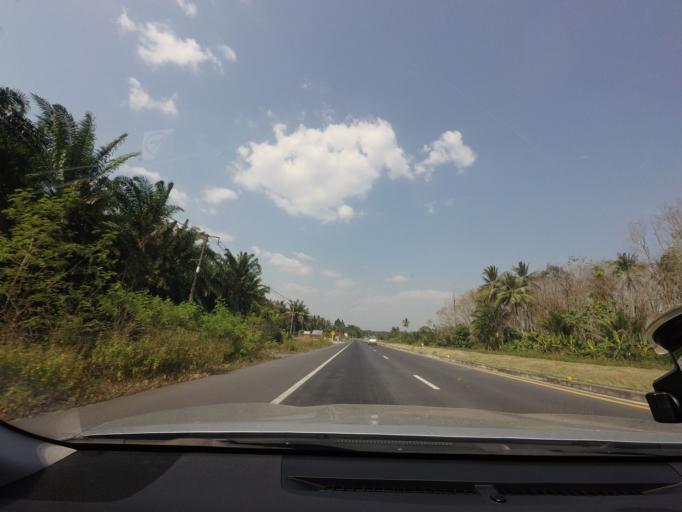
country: TH
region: Phangnga
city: Thap Put
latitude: 8.5354
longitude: 98.7128
